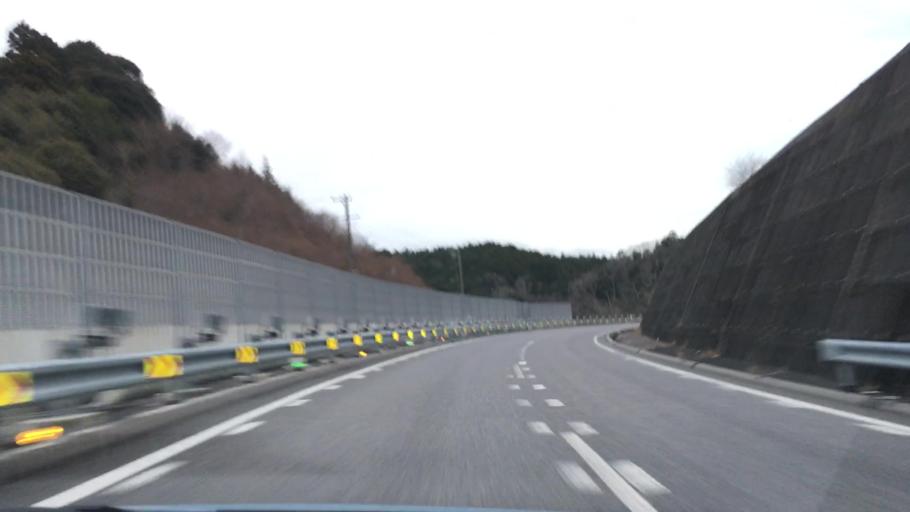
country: JP
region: Aichi
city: Shinshiro
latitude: 34.8921
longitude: 137.6482
